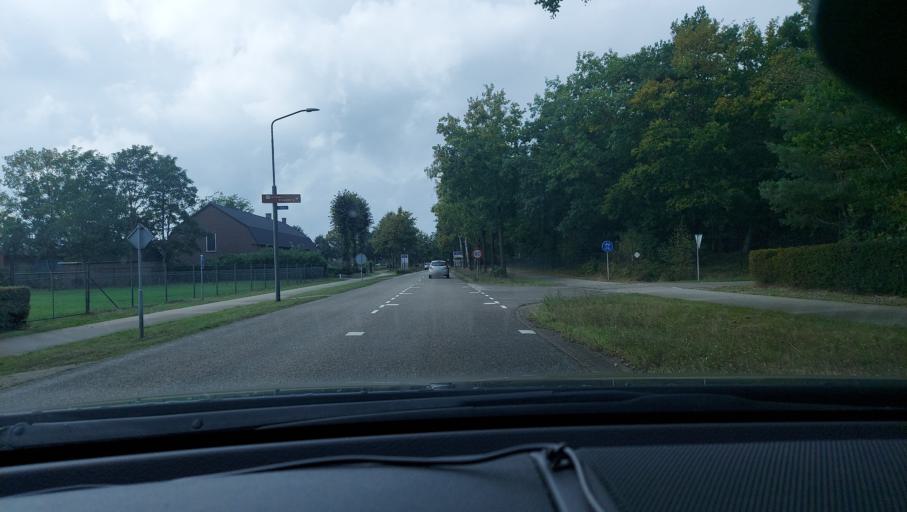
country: NL
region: North Brabant
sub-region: Gemeente Helmond
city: Helmond
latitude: 51.5024
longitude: 5.7553
